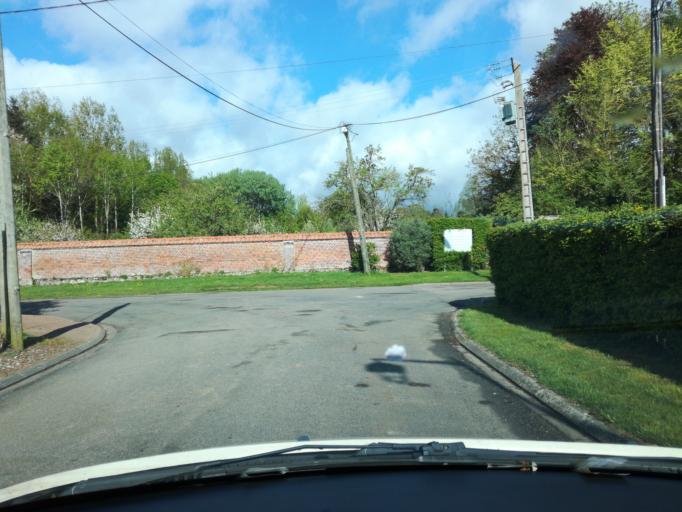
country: FR
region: Picardie
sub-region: Departement de la Somme
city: Poix-de-Picardie
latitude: 49.8206
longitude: 2.0156
